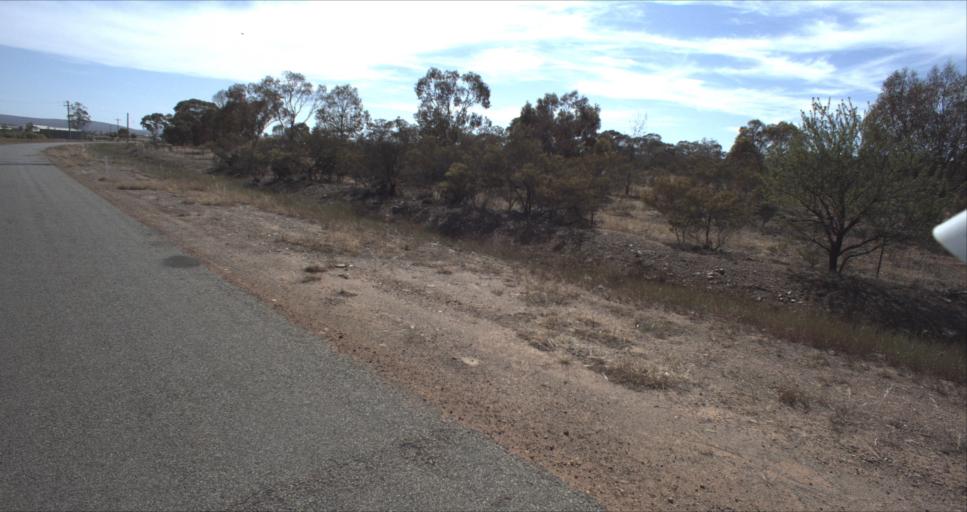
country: AU
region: New South Wales
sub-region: Leeton
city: Leeton
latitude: -34.5797
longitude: 146.4776
